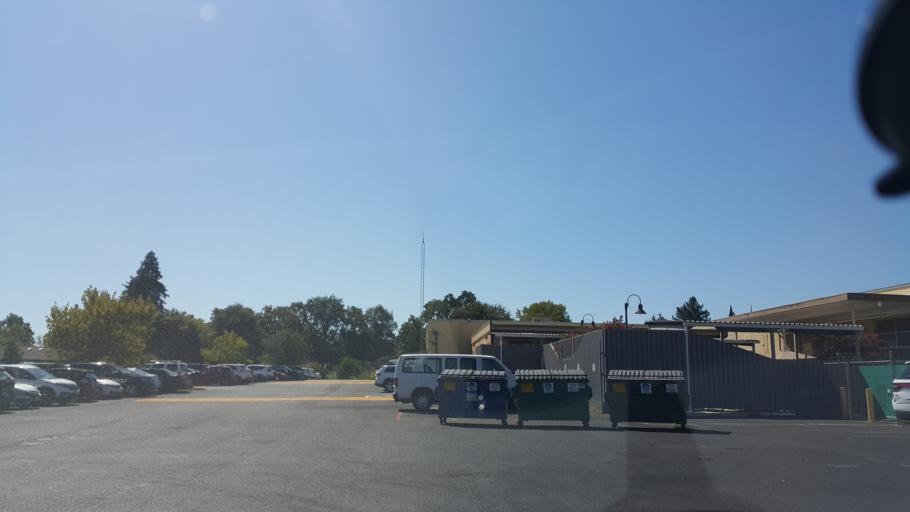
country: US
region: California
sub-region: Mendocino County
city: Ukiah
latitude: 39.1425
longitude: -123.2046
